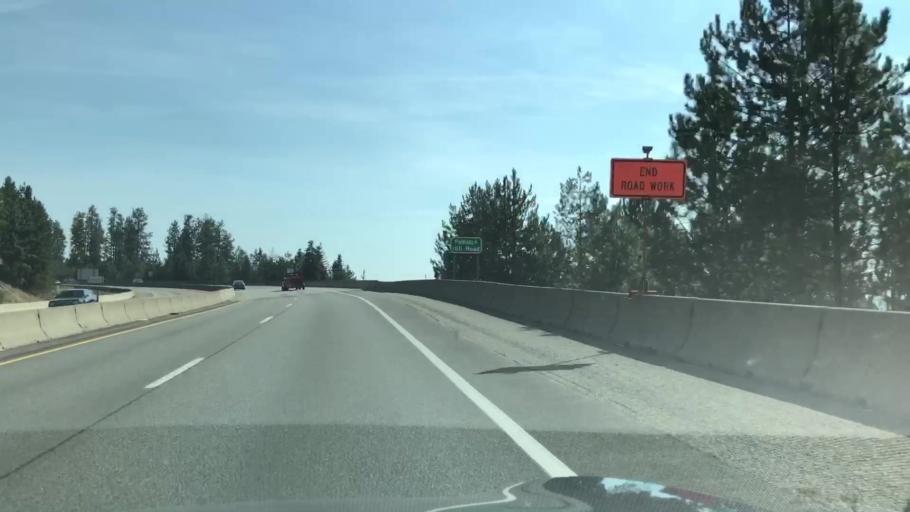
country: US
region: Idaho
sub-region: Kootenai County
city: Coeur d'Alene
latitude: 47.6666
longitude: -116.7508
